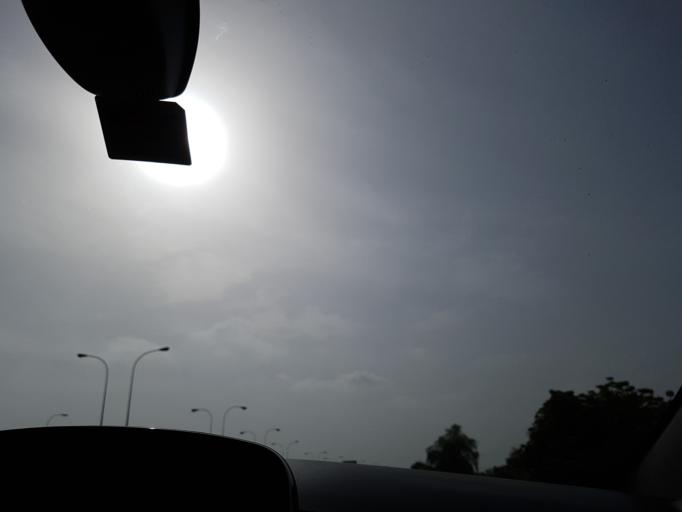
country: OM
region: Al Batinah
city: Al Sohar
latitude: 24.3929
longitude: 56.6917
